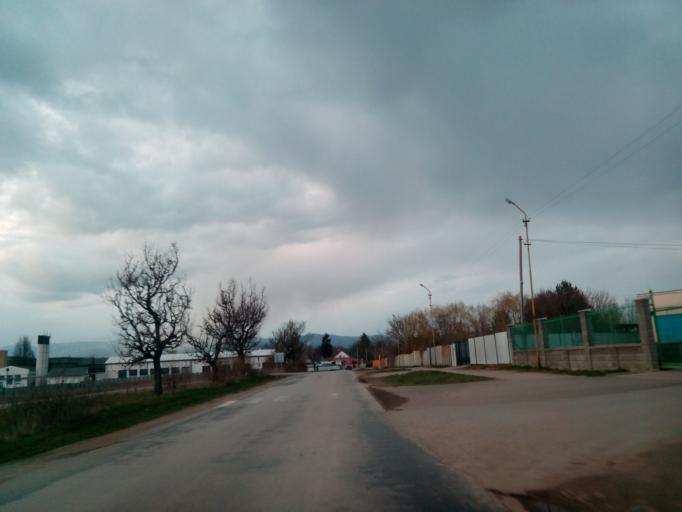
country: SK
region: Kosicky
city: Moldava nad Bodvou
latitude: 48.6014
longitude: 20.9978
